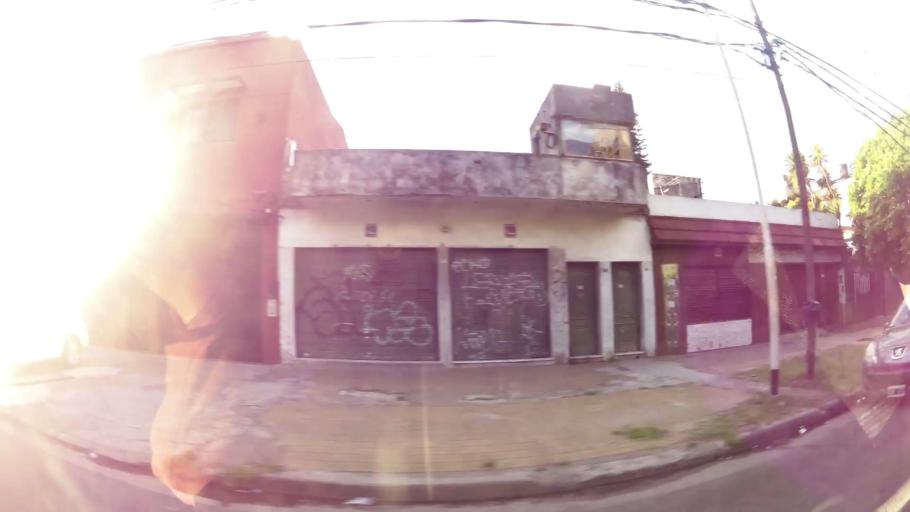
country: AR
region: Buenos Aires
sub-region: Partido de Avellaneda
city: Avellaneda
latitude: -34.6948
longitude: -58.3311
